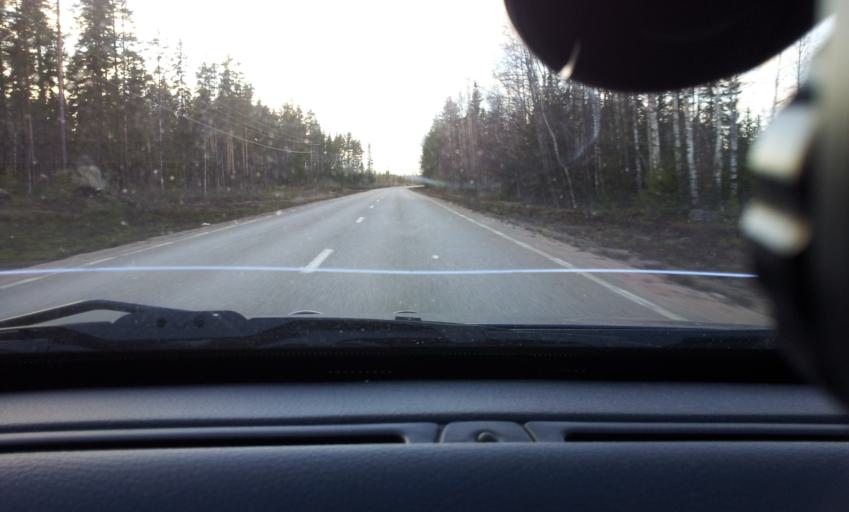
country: SE
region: Jaemtland
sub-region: Harjedalens Kommun
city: Sveg
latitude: 62.0992
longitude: 15.0757
